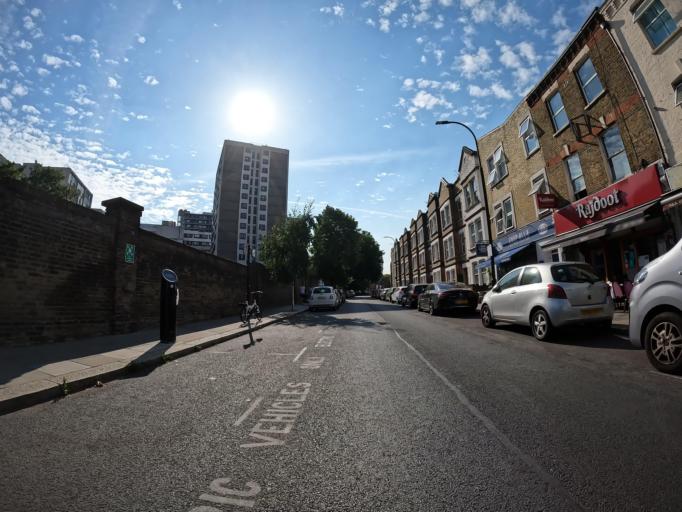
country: GB
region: England
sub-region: Greater London
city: Hendon
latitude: 51.5841
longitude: -0.2174
